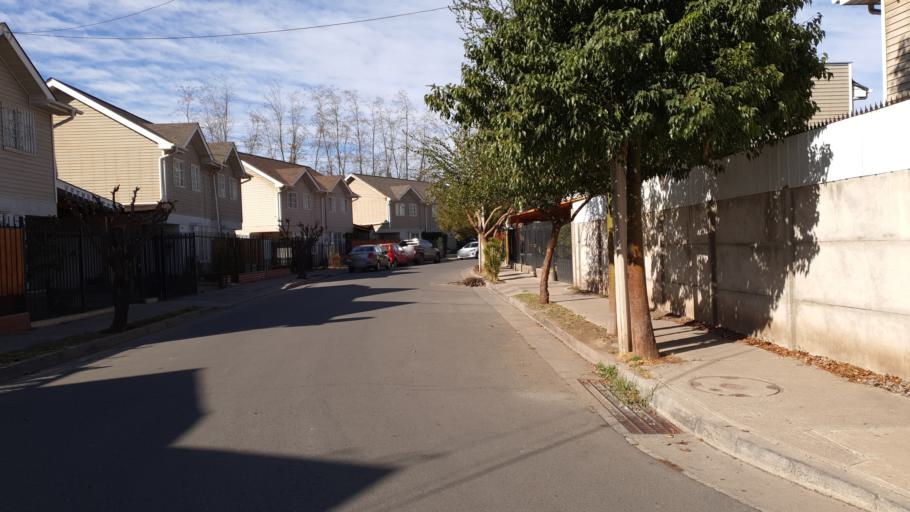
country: CL
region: Valparaiso
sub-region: Provincia de Los Andes
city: Los Andes
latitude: -32.8278
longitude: -70.5941
